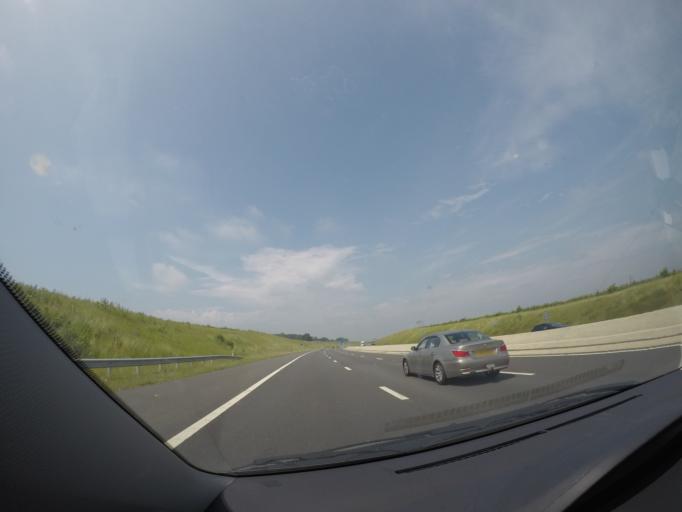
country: GB
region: England
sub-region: North Yorkshire
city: Catterick
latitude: 54.3617
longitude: -1.6252
